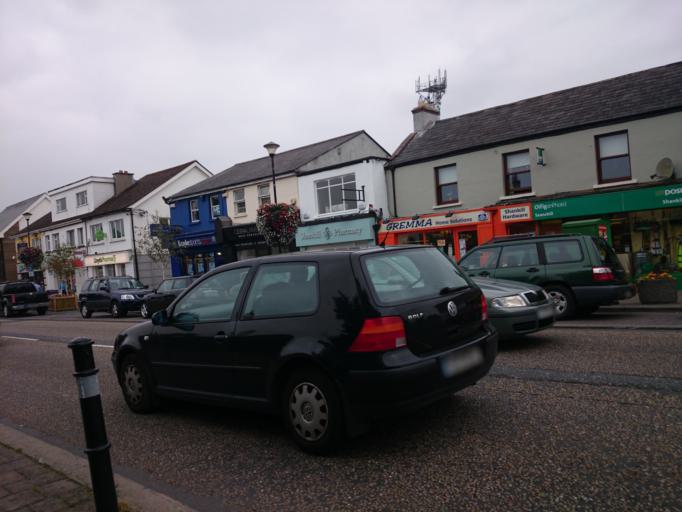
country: IE
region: Leinster
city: Shankill
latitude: 53.2312
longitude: -6.1240
